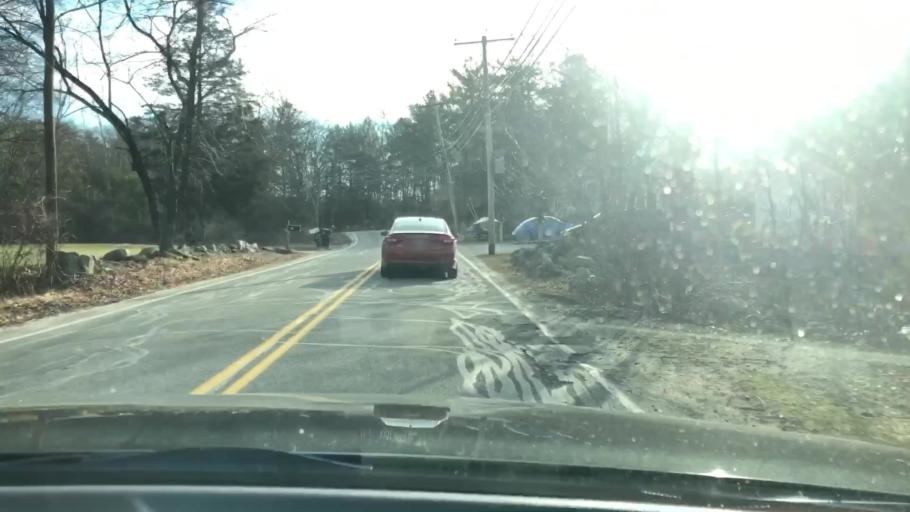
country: US
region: Massachusetts
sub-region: Worcester County
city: Milford
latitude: 42.1140
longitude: -71.5150
